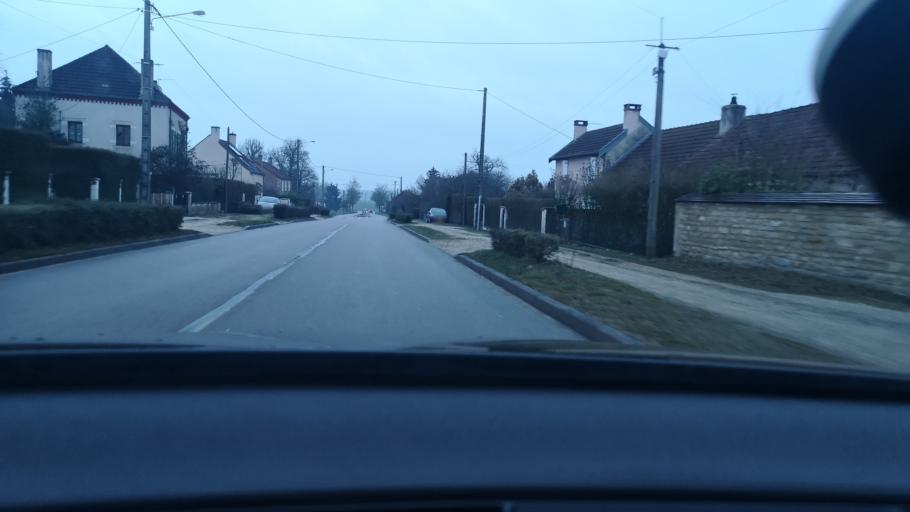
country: FR
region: Bourgogne
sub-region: Departement de la Cote-d'Or
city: Seurre
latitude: 47.0652
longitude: 5.0967
